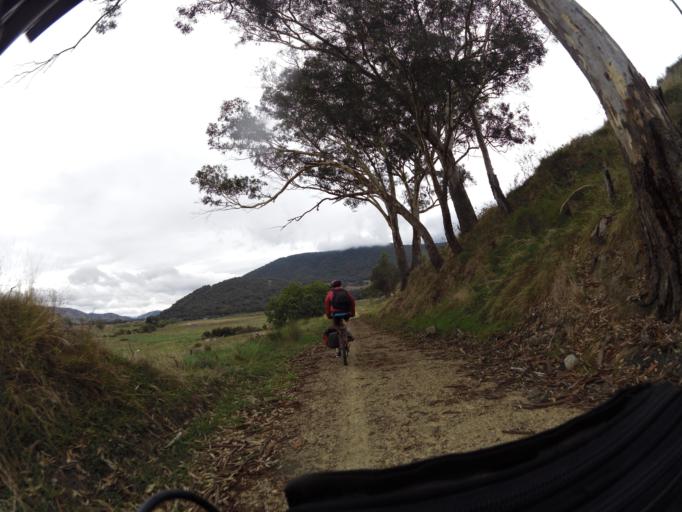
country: AU
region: New South Wales
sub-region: Albury Municipality
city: East Albury
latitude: -36.1840
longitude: 147.3524
